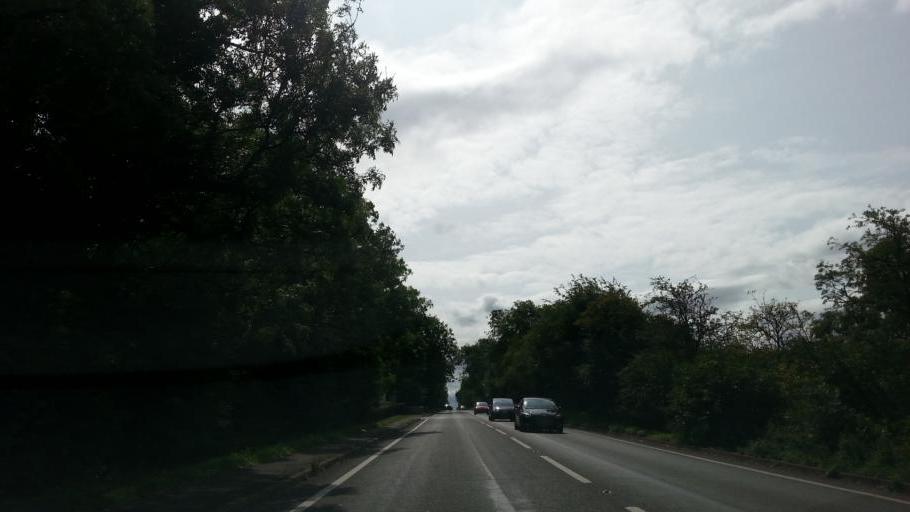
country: GB
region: England
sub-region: Leicestershire
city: Market Harborough
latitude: 52.5054
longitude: -0.9403
